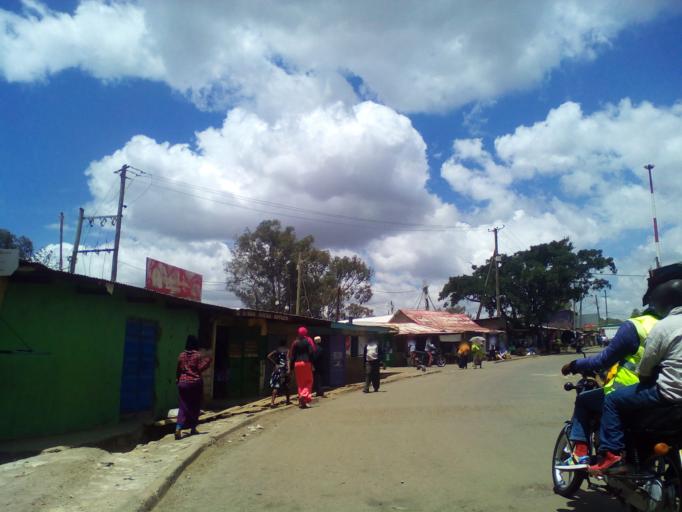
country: KE
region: Nairobi Area
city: Nairobi
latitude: -1.3097
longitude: 36.7858
